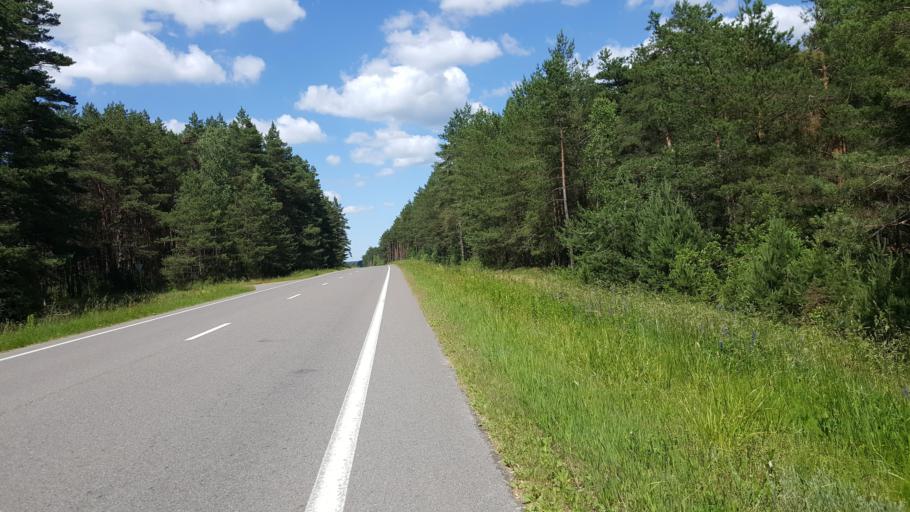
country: PL
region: Podlasie
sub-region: Powiat hajnowski
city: Czeremcha
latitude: 52.5198
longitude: 23.5348
